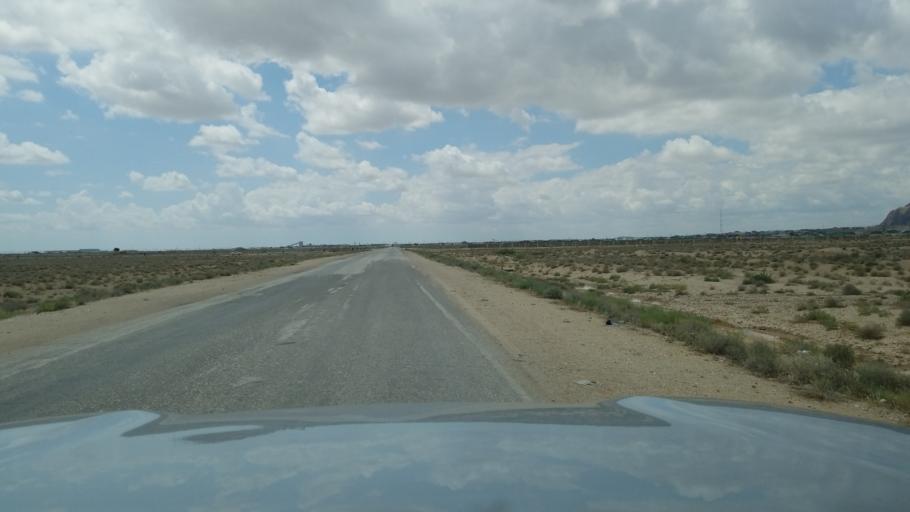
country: TM
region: Balkan
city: Balkanabat
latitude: 39.4872
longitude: 54.4146
